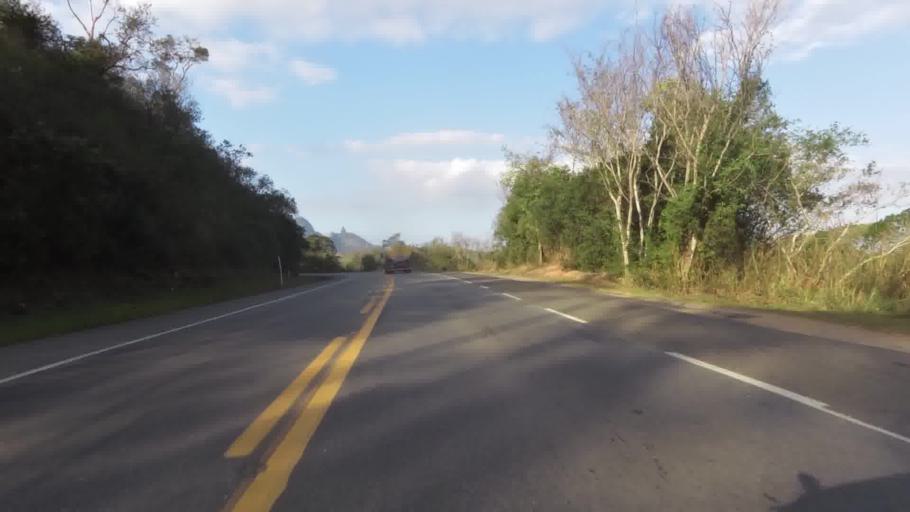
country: BR
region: Espirito Santo
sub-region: Cachoeiro De Itapemirim
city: Cachoeiro de Itapemirim
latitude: -20.9031
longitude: -41.0599
